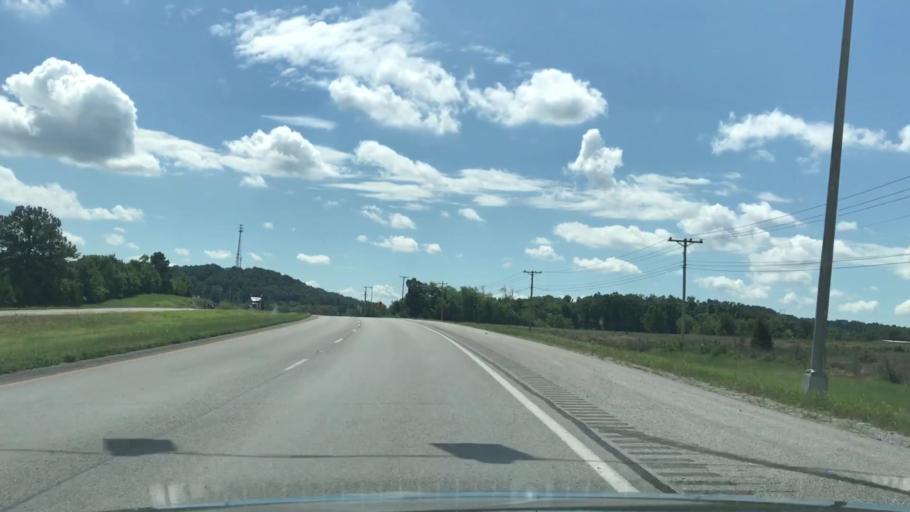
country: US
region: Kentucky
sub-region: Logan County
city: Russellville
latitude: 36.8428
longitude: -86.9200
